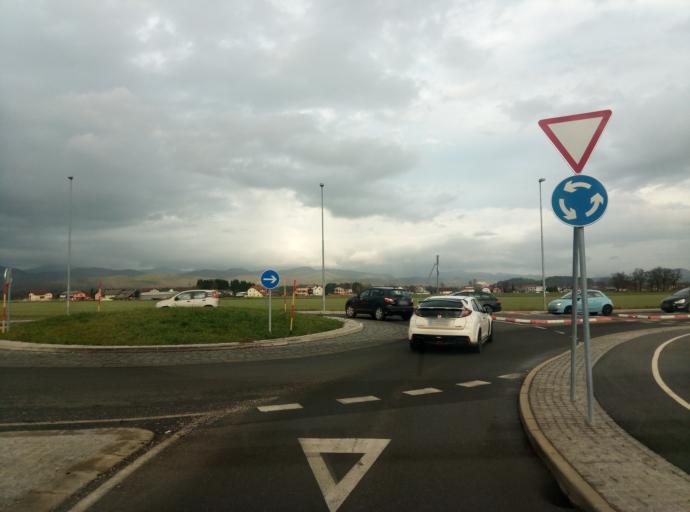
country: SI
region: Domzale
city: Vir
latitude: 46.1511
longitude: 14.6149
